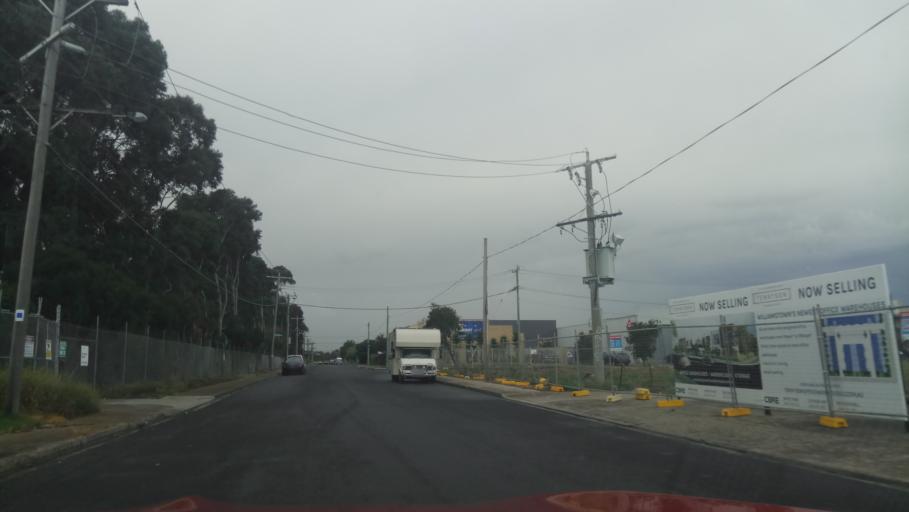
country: AU
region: Victoria
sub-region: Hobsons Bay
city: Seaholme
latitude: -37.8521
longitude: 144.8582
